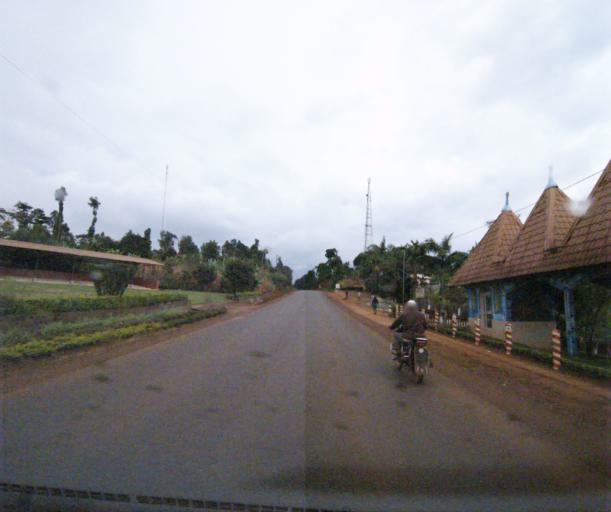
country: CM
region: West
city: Dschang
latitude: 5.4895
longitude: 10.1797
